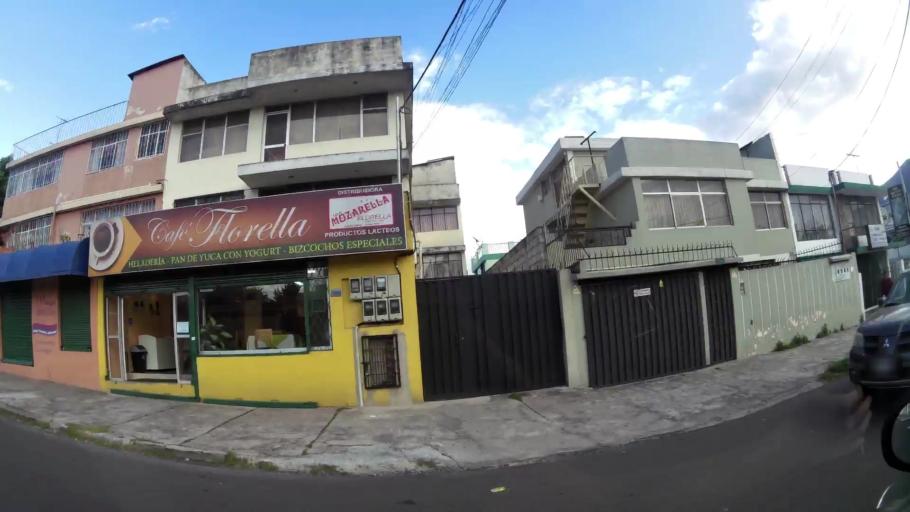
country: EC
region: Pichincha
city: Quito
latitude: -0.1412
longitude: -78.4817
